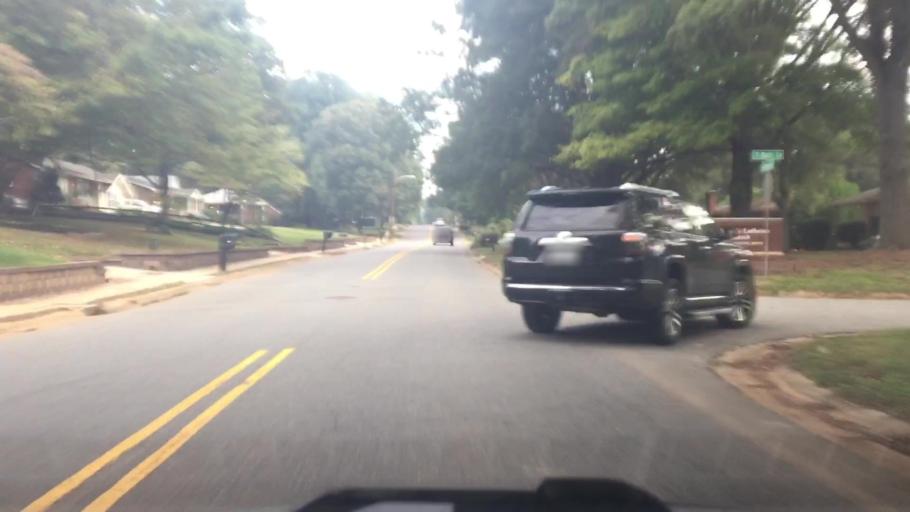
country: US
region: North Carolina
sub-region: Iredell County
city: Mooresville
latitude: 35.5689
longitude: -80.8001
